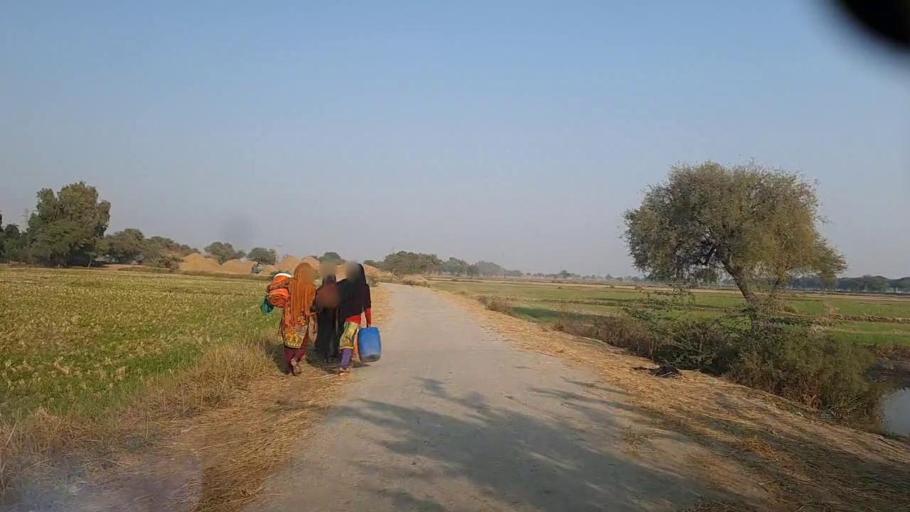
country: PK
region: Sindh
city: Jacobabad
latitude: 28.2385
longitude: 68.4871
